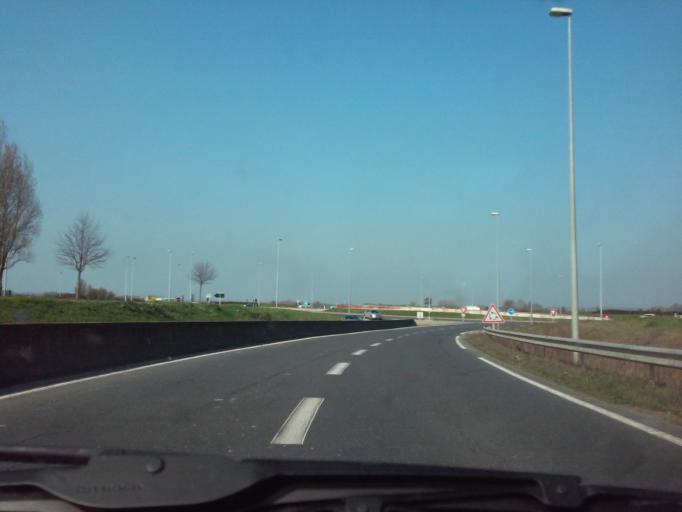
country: FR
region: Lower Normandy
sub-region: Departement du Calvados
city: Saint-Vigor-le-Grand
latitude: 49.2554
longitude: -0.6480
